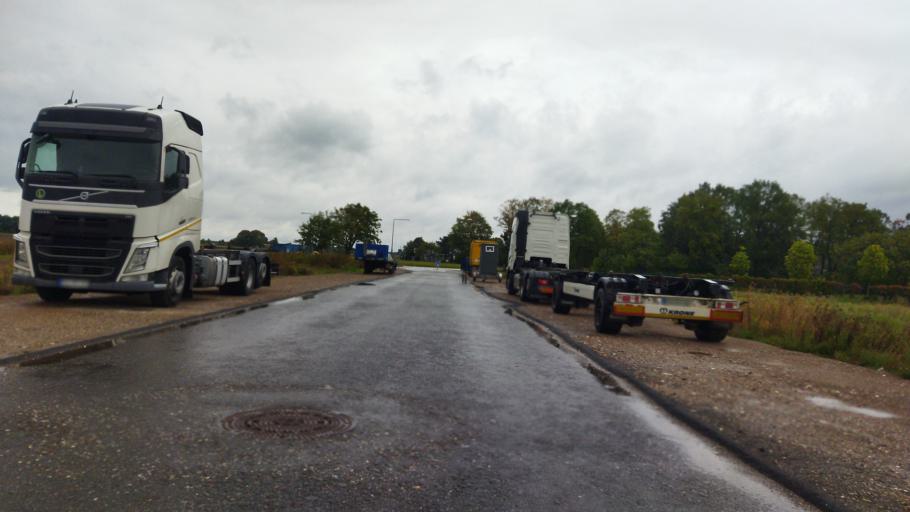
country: DE
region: North Rhine-Westphalia
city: Wesseling
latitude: 50.8620
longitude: 6.9642
